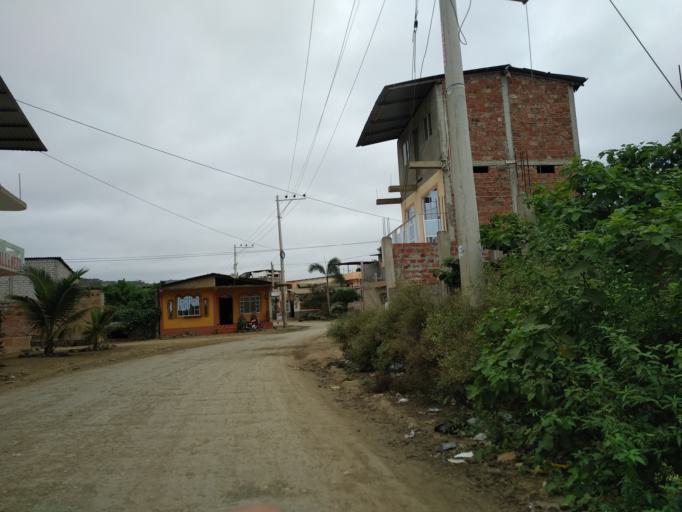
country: EC
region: Manabi
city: Jipijapa
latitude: -1.5524
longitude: -80.8094
